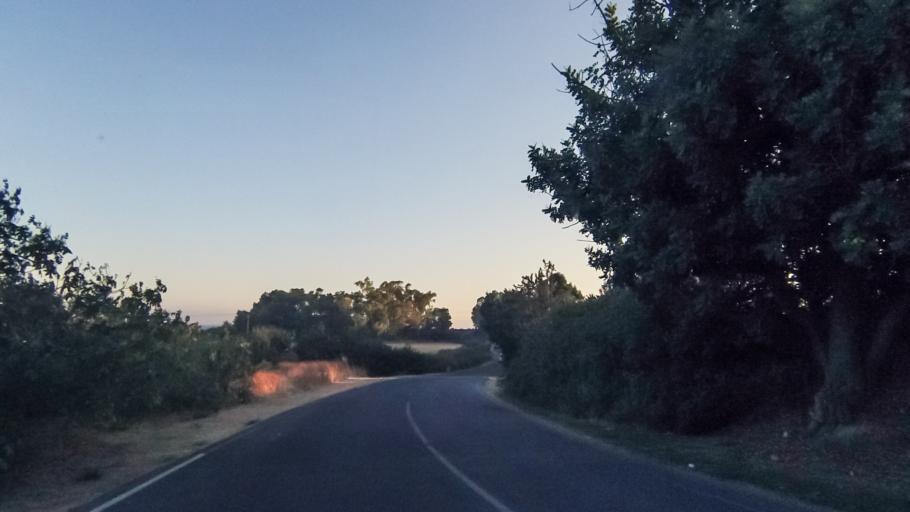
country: CY
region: Limassol
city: Erimi
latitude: 34.6644
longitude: 32.8945
